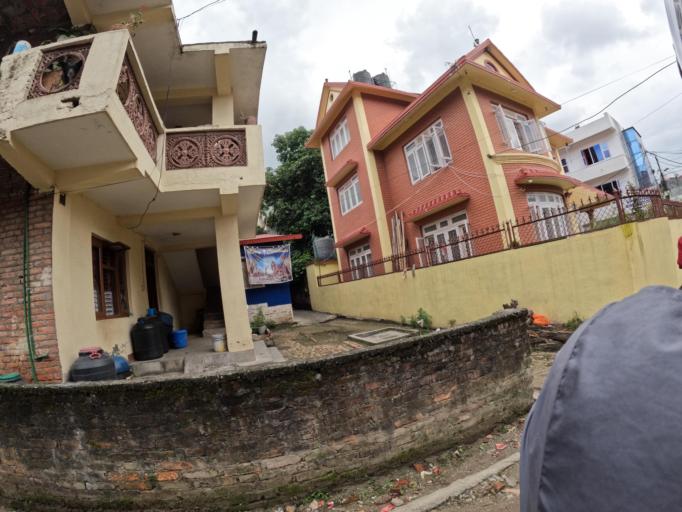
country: NP
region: Central Region
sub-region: Bagmati Zone
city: Kathmandu
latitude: 27.7402
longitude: 85.3175
